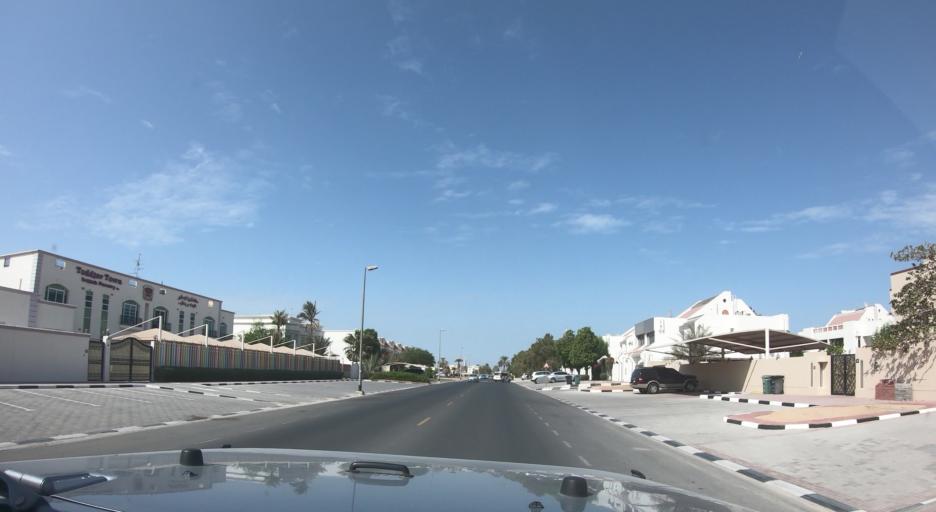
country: AE
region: Dubai
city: Dubai
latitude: 25.1605
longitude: 55.2241
